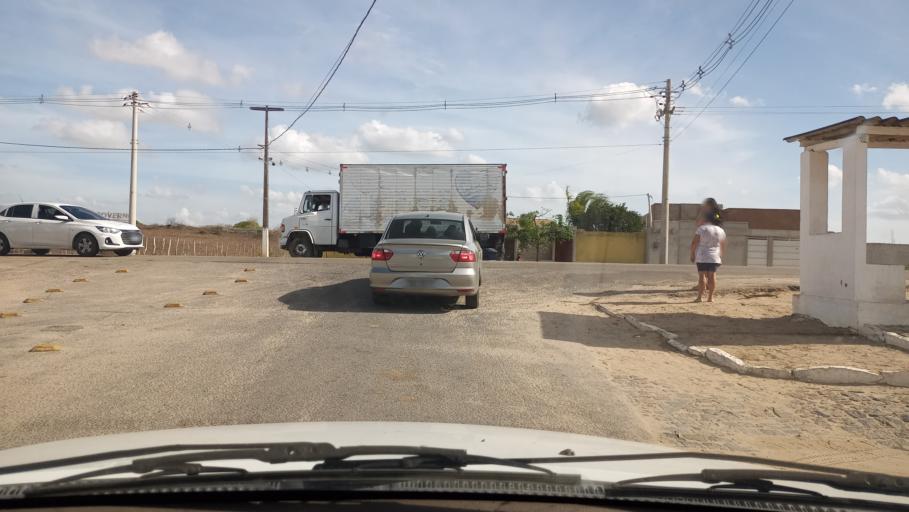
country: BR
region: Rio Grande do Norte
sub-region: Goianinha
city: Goianinha
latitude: -6.3356
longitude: -35.3001
